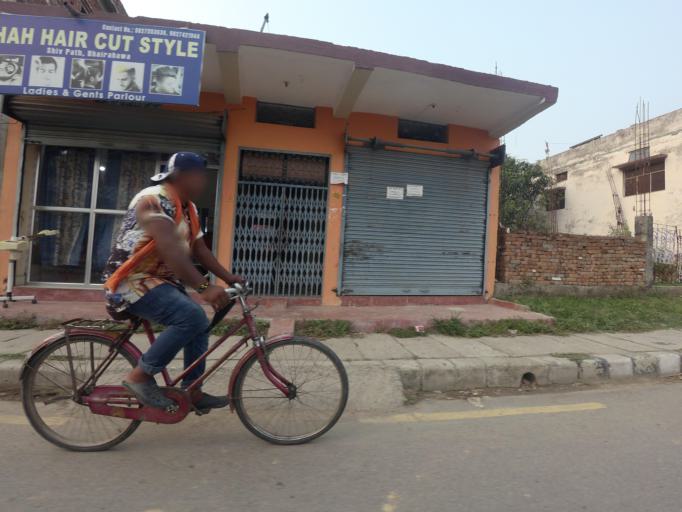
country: NP
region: Western Region
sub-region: Lumbini Zone
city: Bhairahawa
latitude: 27.5146
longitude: 83.4473
